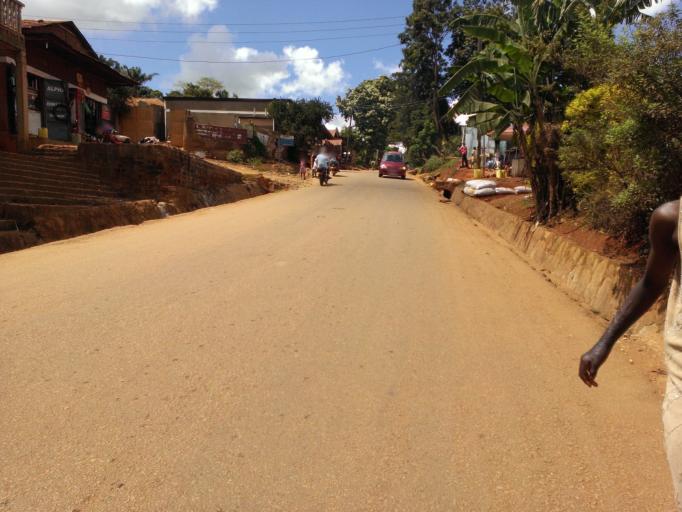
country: UG
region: Central Region
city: Kampala Central Division
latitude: 0.3222
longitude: 32.5545
